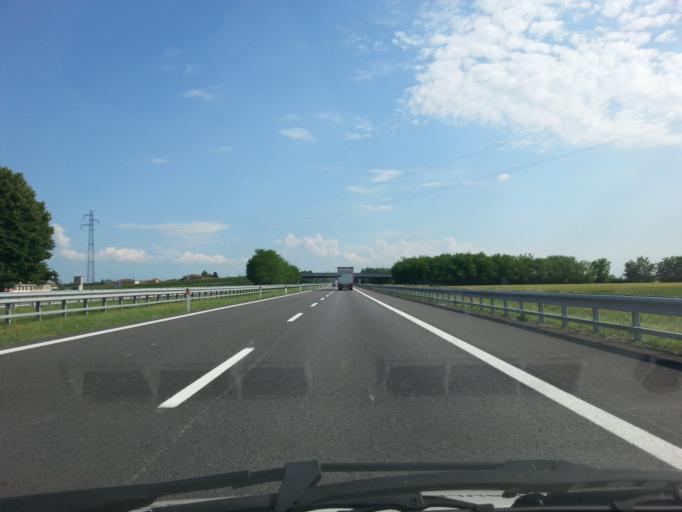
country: IT
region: Piedmont
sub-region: Provincia di Cuneo
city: Caramagna Piemonte
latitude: 44.8212
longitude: 7.7508
